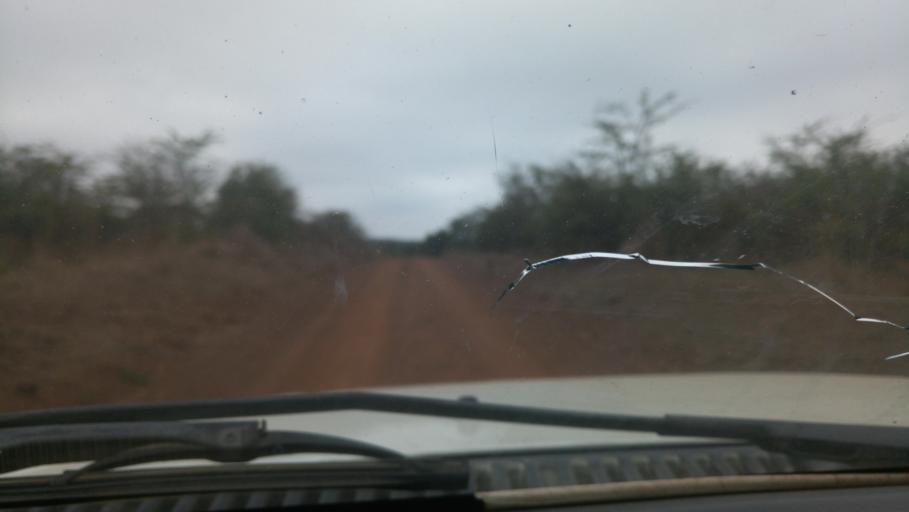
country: KE
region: Nairobi Area
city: Nairobi
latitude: -1.3837
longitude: 36.7852
